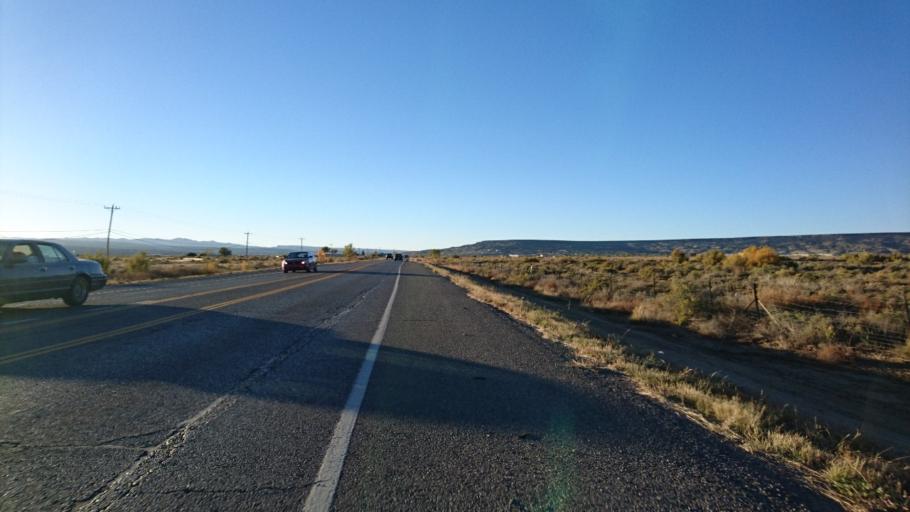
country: US
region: New Mexico
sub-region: Cibola County
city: Grants
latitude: 35.1312
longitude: -107.8115
